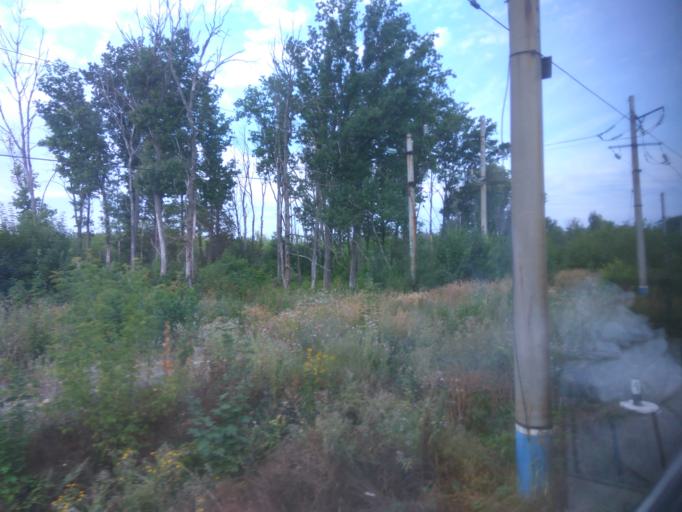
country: RU
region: Saratov
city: Rtishchevo
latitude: 52.2224
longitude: 43.8625
